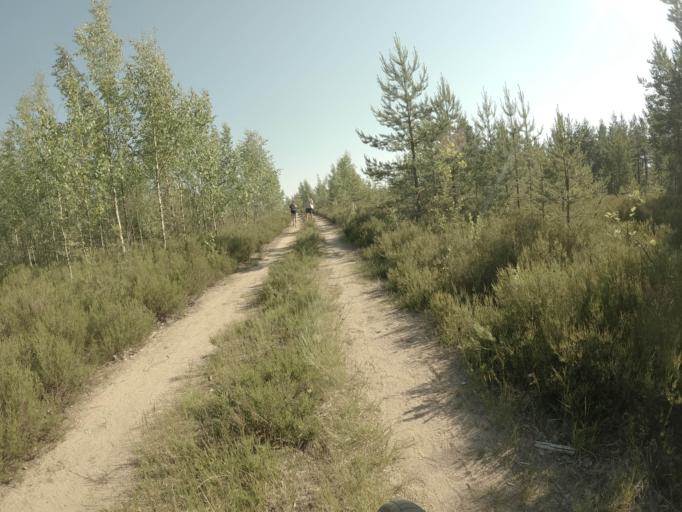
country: RU
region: Leningrad
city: Yakovlevo
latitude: 60.4442
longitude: 29.2398
